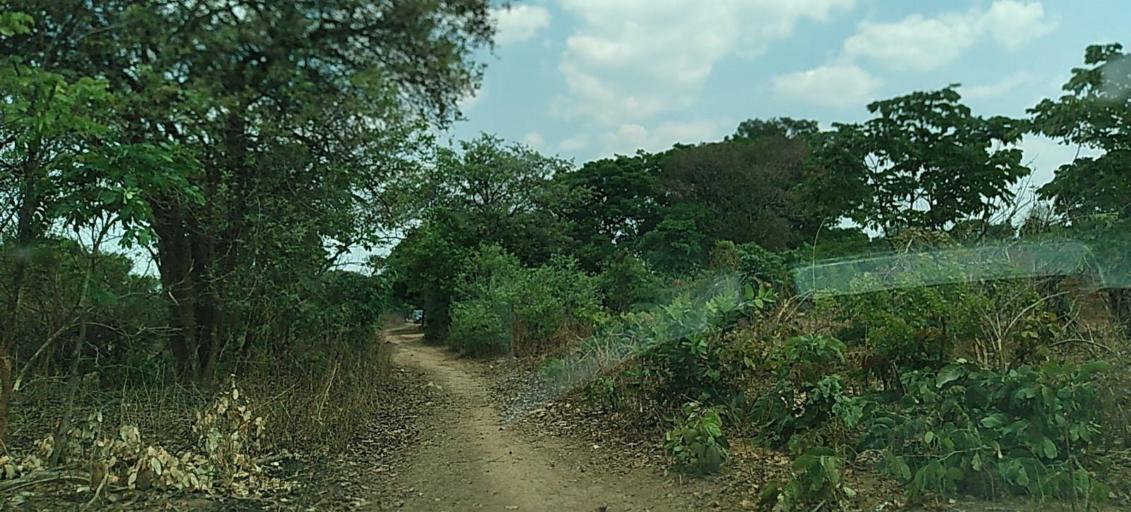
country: CD
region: Katanga
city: Kipushi
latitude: -12.0384
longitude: 27.4371
